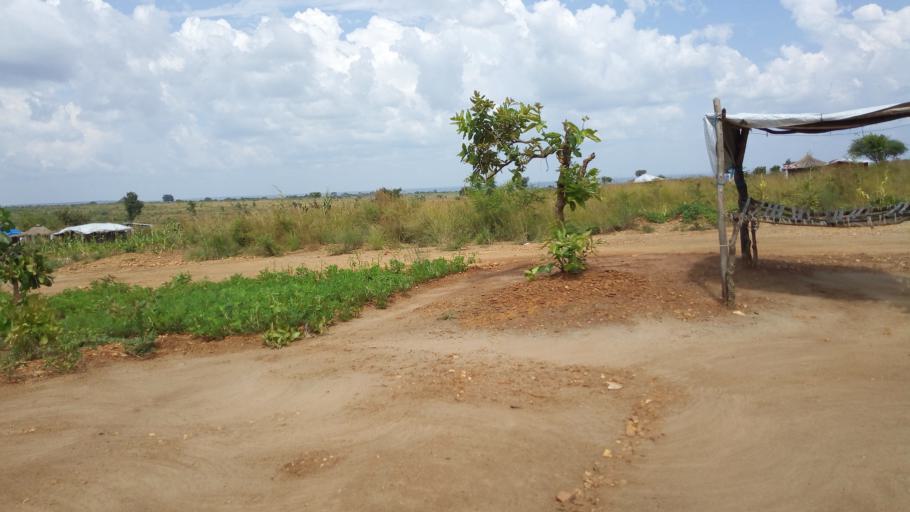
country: UG
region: Northern Region
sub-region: Yumbe District
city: Yumbe
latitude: 3.5264
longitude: 31.3410
